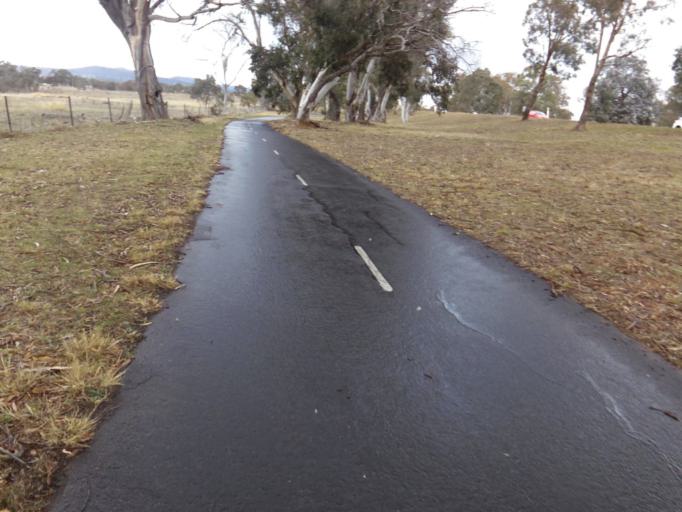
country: AU
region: Australian Capital Territory
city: Macquarie
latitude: -35.2719
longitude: 149.0759
